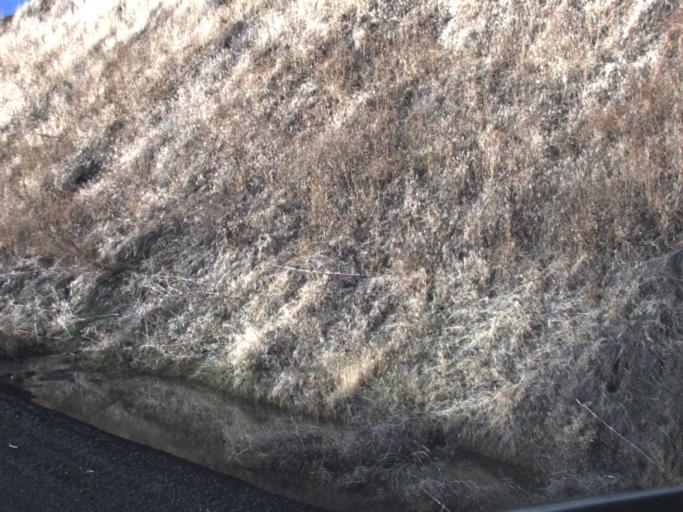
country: US
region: Washington
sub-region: Whitman County
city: Colfax
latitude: 46.7569
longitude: -117.4544
